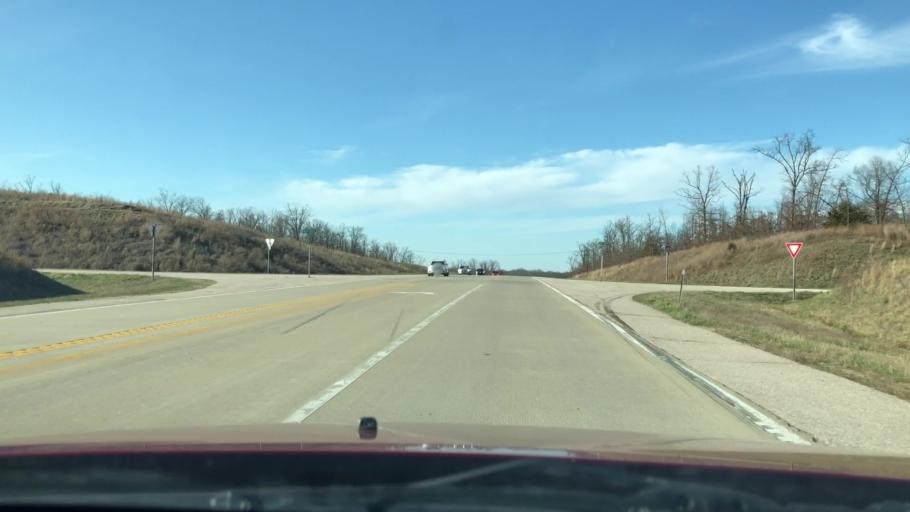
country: US
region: Missouri
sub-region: Camden County
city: Camdenton
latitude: 37.9351
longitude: -92.7149
